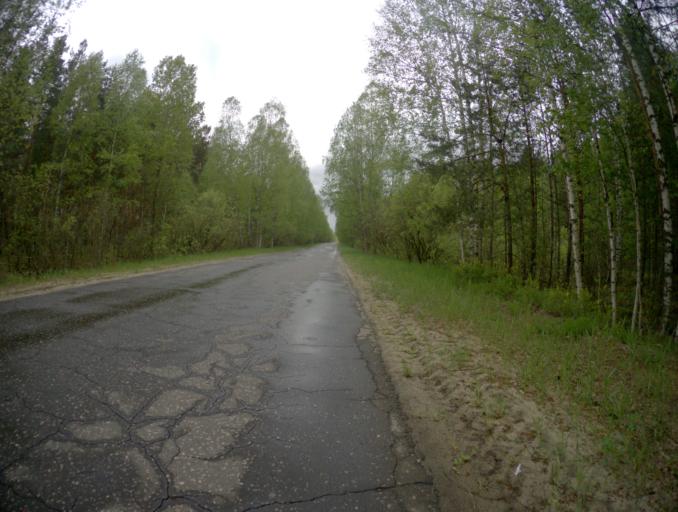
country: RU
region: Vladimir
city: Zolotkovo
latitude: 55.3503
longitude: 40.9308
